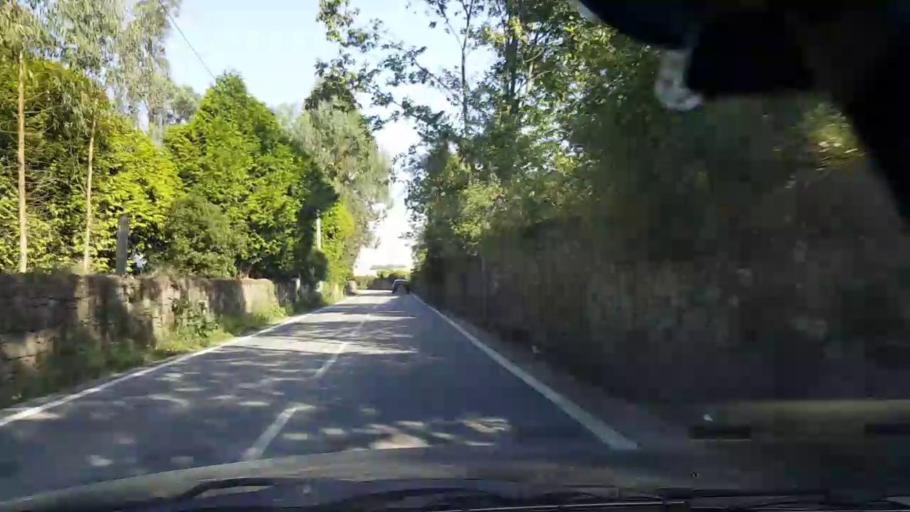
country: PT
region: Porto
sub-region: Vila do Conde
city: Arvore
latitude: 41.3196
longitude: -8.6796
